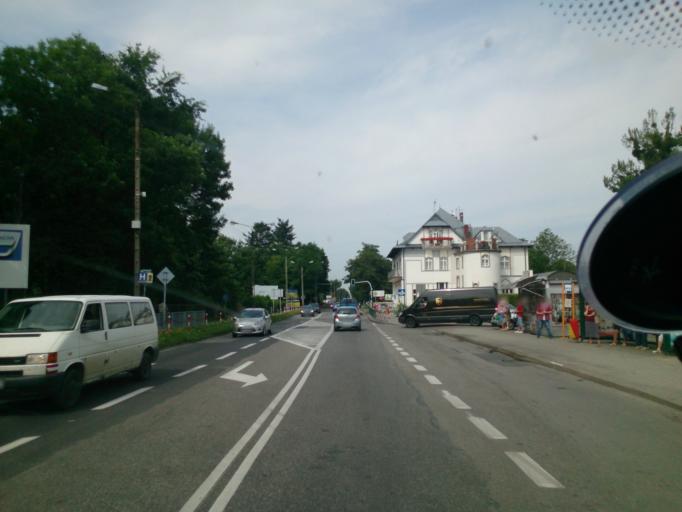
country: PL
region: Silesian Voivodeship
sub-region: Powiat bielski
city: Jaworze
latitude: 49.8080
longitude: 18.9842
